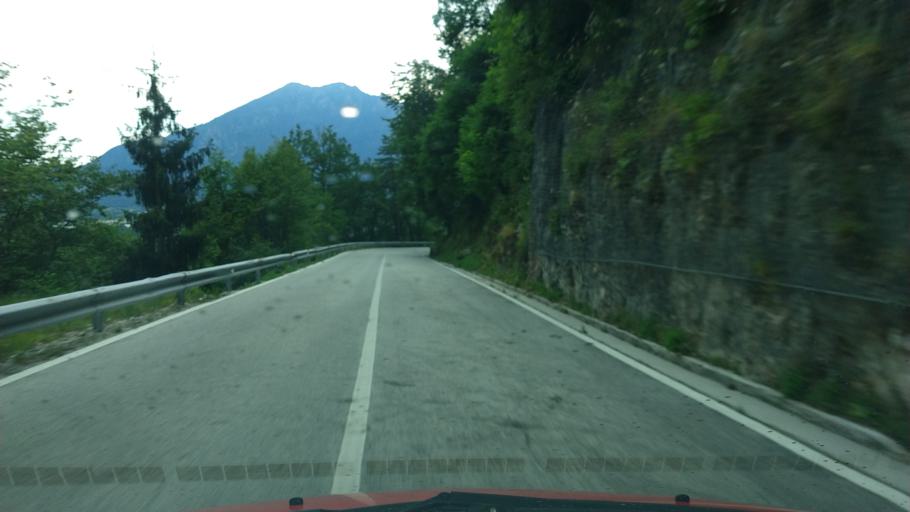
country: IT
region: Veneto
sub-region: Provincia di Vicenza
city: Arsiero
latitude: 45.8154
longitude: 11.3583
